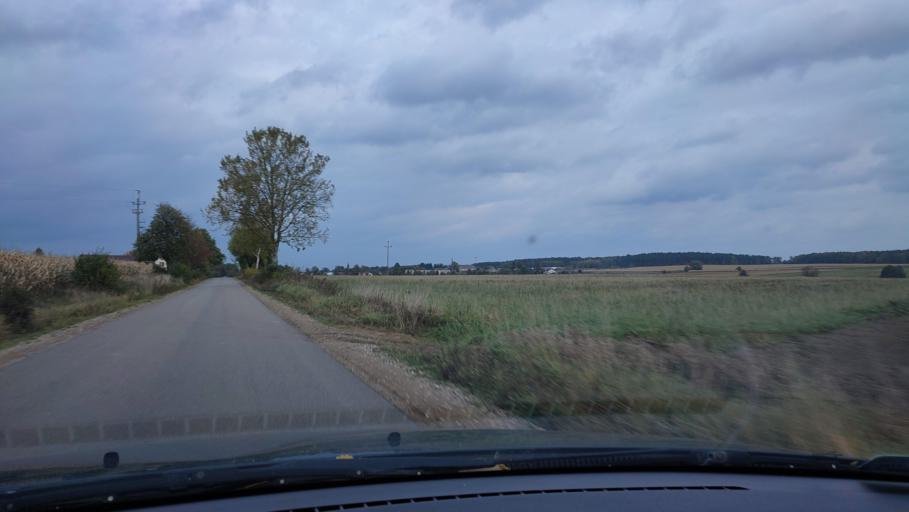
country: PL
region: Masovian Voivodeship
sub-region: Powiat mlawski
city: Wieczfnia Koscielna
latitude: 53.2044
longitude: 20.3897
